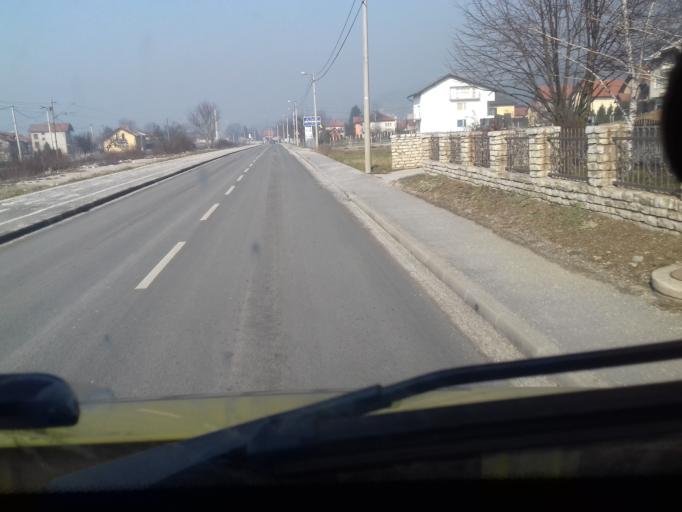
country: BA
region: Federation of Bosnia and Herzegovina
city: Mahala
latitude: 43.9804
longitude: 18.2402
